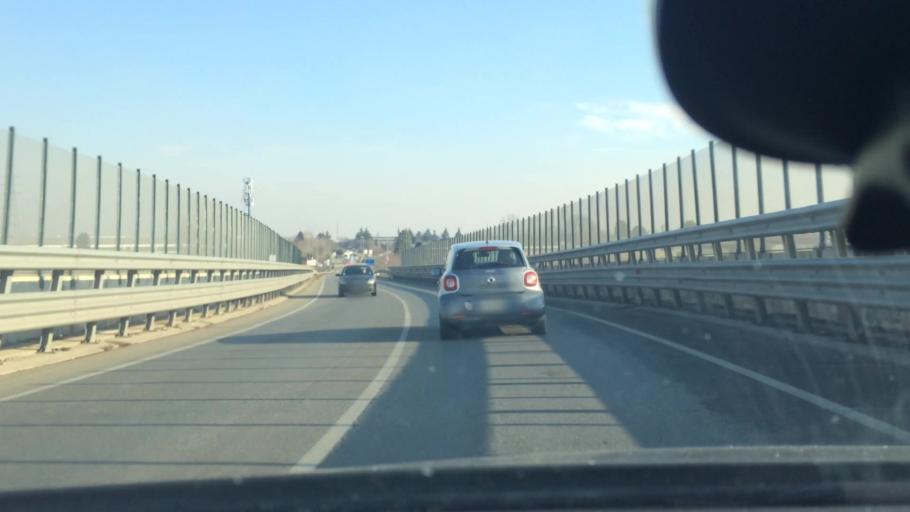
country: IT
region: Lombardy
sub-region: Citta metropolitana di Milano
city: Arluno
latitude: 45.4989
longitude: 8.9309
